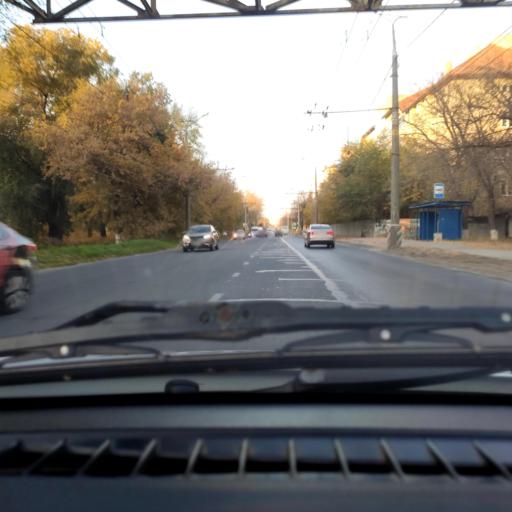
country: RU
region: Samara
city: Tol'yatti
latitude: 53.5214
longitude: 49.4330
